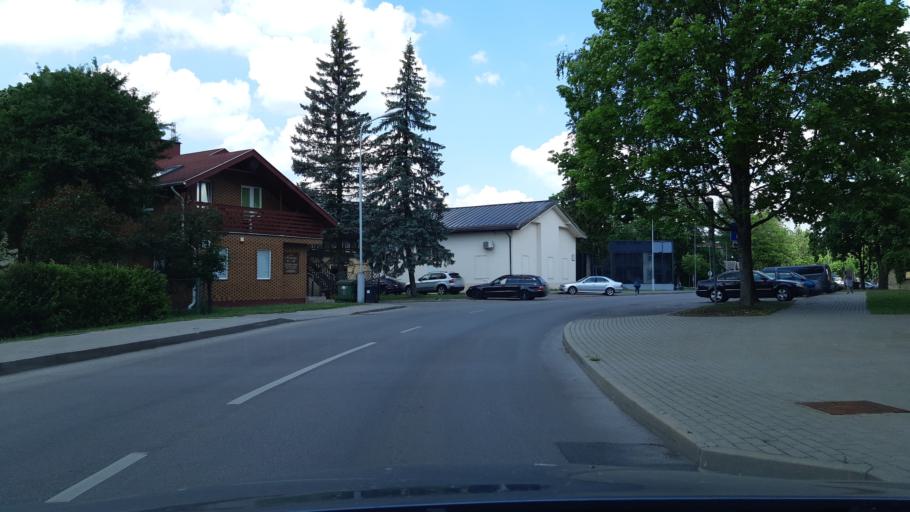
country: LT
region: Alytaus apskritis
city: Druskininkai
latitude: 54.0133
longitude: 23.9819
